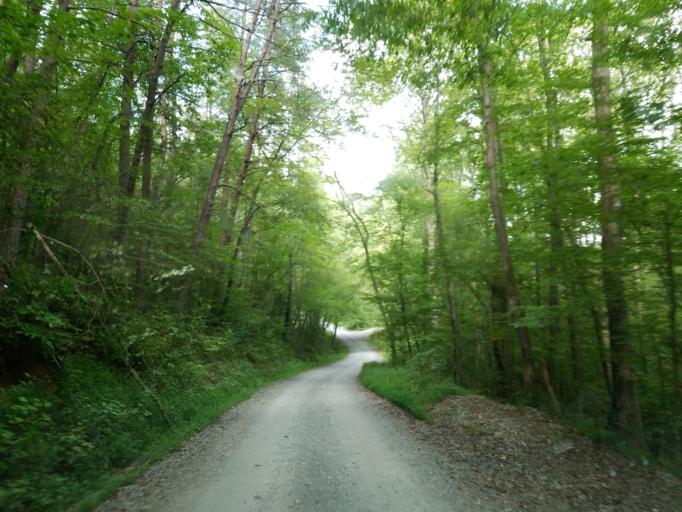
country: US
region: Georgia
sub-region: Gilmer County
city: Ellijay
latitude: 34.7820
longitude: -84.4242
